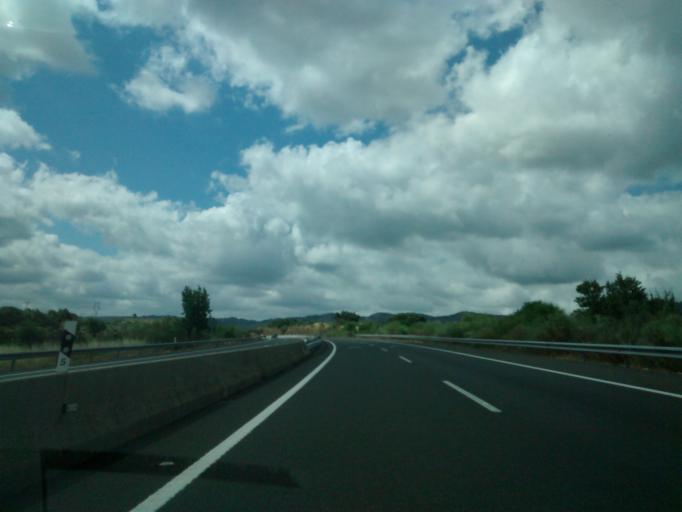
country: ES
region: Extremadura
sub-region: Provincia de Caceres
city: Romangordo
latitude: 39.7478
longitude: -5.7267
